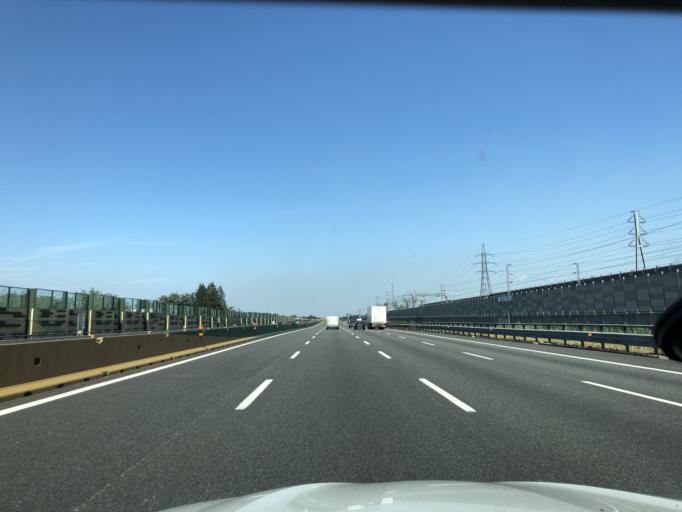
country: IT
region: Lombardy
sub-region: Citta metropolitana di Milano
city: Vittuone
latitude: 45.5020
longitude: 8.9583
